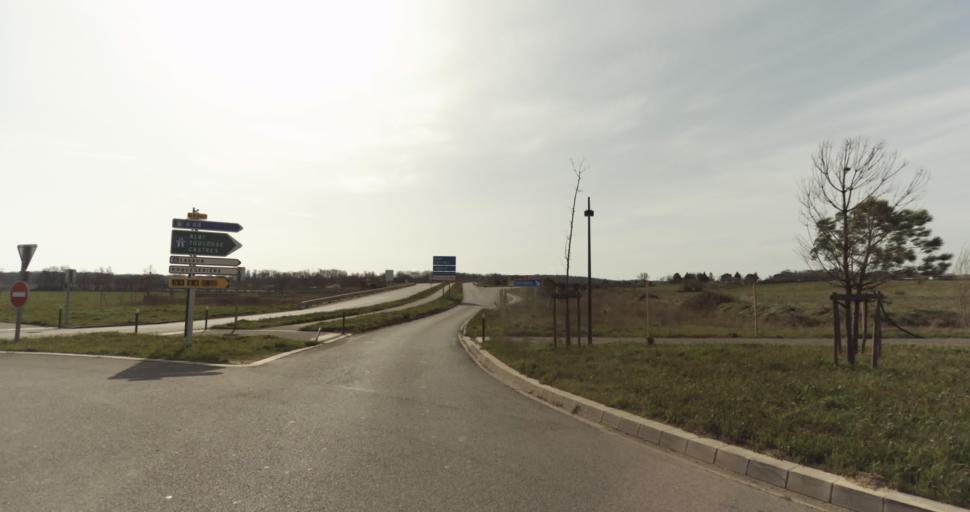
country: FR
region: Midi-Pyrenees
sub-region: Departement du Tarn
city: Saint-Sulpice-la-Pointe
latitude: 43.7567
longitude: 1.6588
